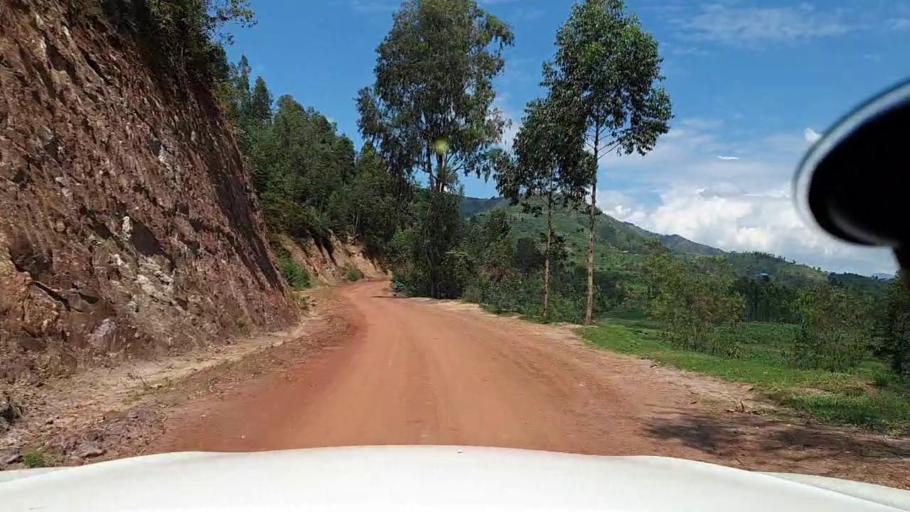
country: RW
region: Kigali
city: Kigali
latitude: -1.7801
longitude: 29.8780
